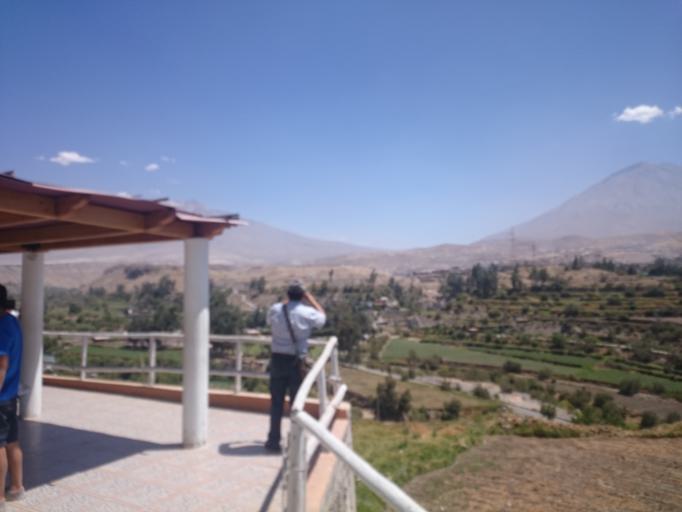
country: PE
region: Arequipa
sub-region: Provincia de Arequipa
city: Arequipa
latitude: -16.3700
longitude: -71.5363
